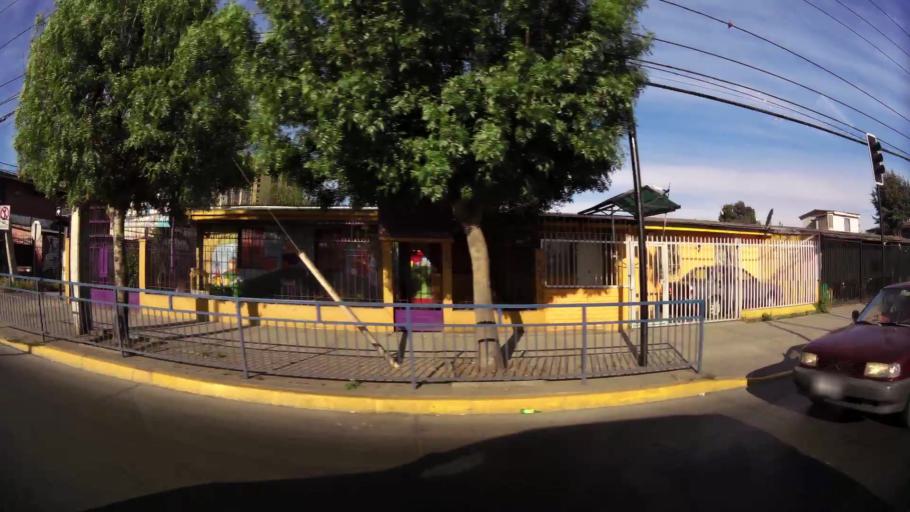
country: CL
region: Santiago Metropolitan
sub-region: Provincia de Santiago
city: Lo Prado
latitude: -33.4614
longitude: -70.7052
